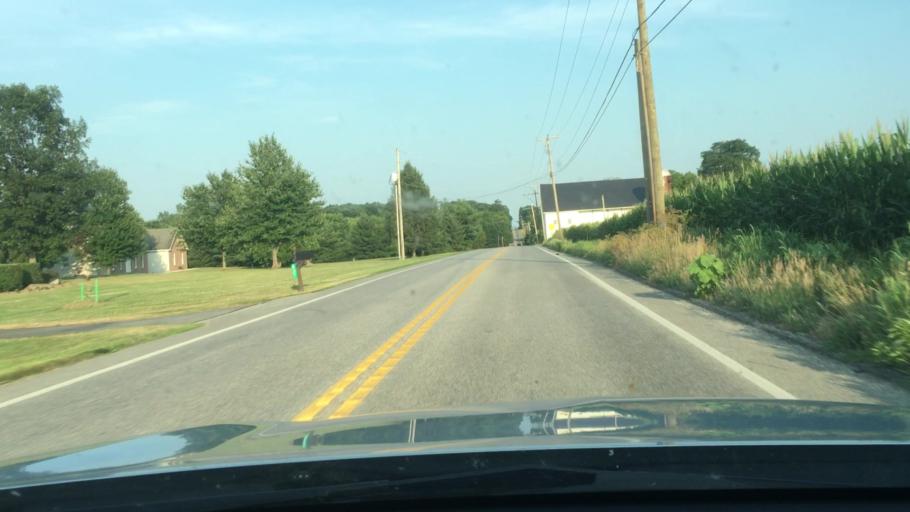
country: US
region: Pennsylvania
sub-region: Cumberland County
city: Boiling Springs
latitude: 40.1756
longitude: -77.1267
